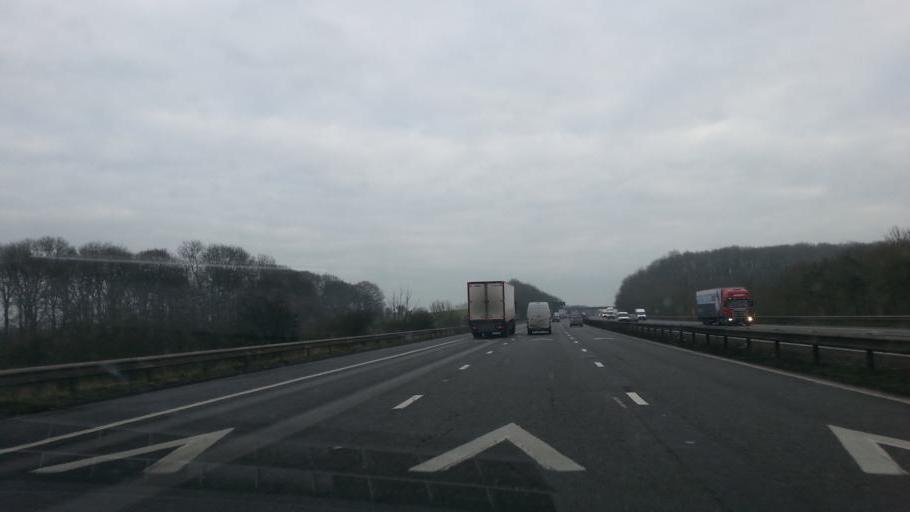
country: GB
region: England
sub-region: Warwickshire
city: Long Lawford
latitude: 52.4295
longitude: -1.3247
